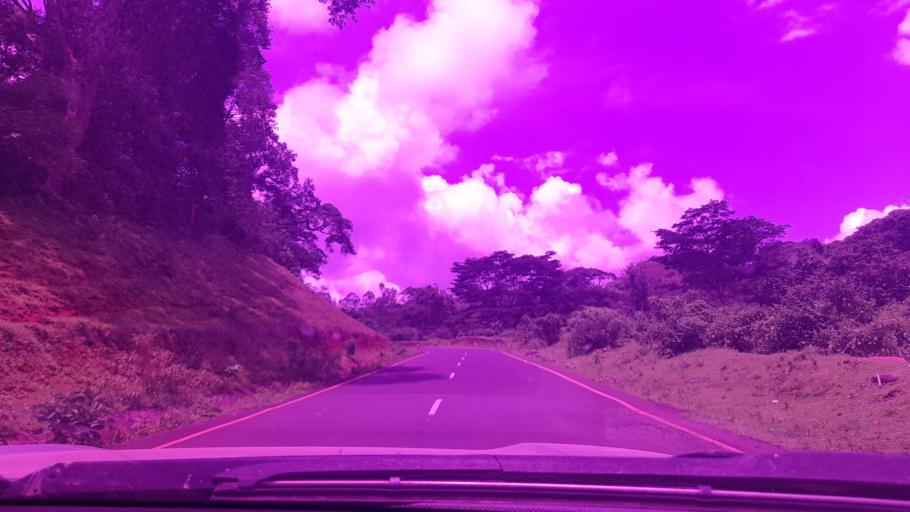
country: ET
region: Oromiya
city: Metu
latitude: 8.3381
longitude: 35.7402
